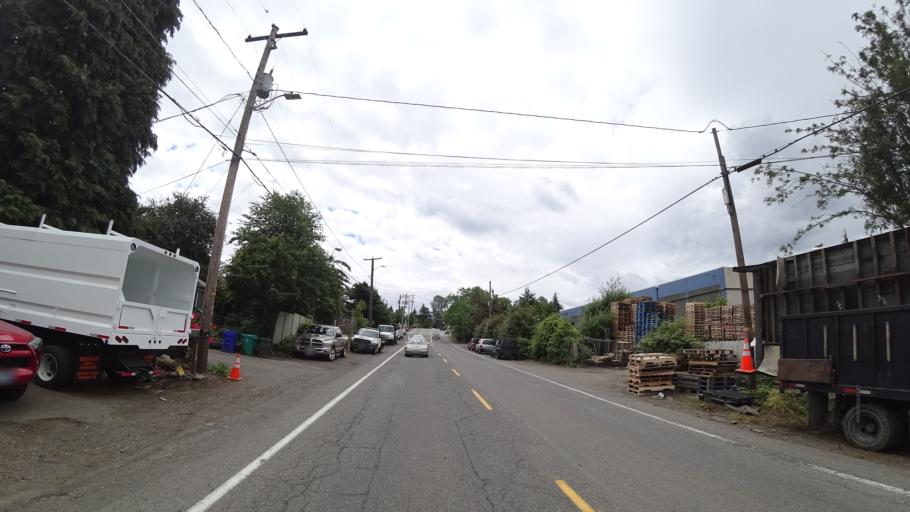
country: US
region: Oregon
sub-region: Multnomah County
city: Portland
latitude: 45.5725
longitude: -122.6141
